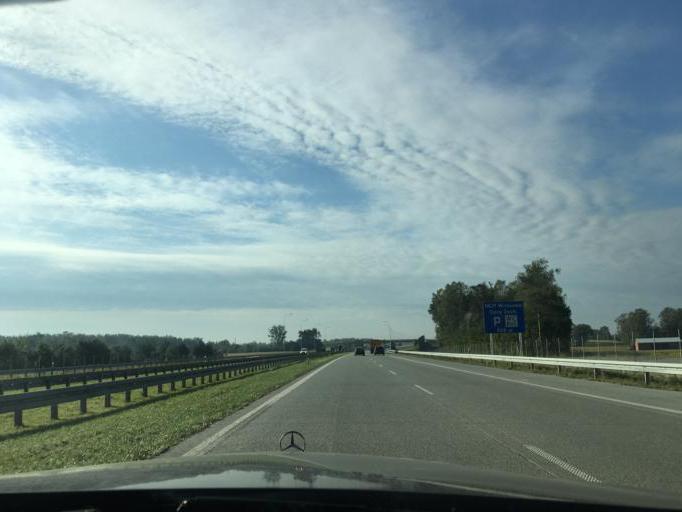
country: PL
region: Lodz Voivodeship
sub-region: Powiat lodzki wschodni
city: Andrespol
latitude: 51.7120
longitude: 19.6076
